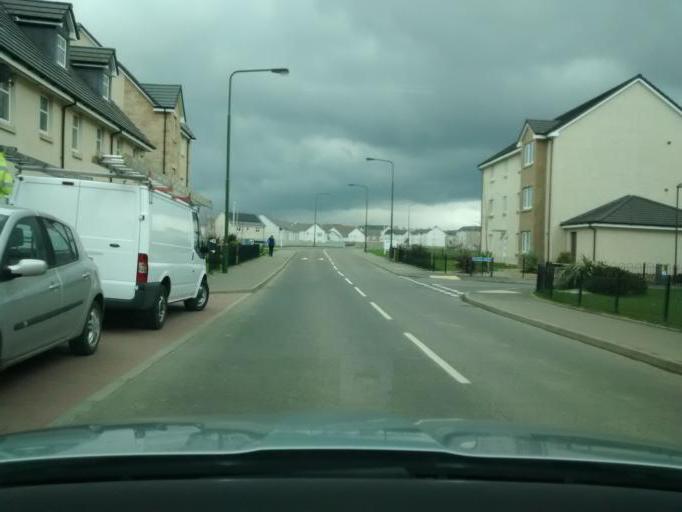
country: GB
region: Scotland
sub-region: West Lothian
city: Bathgate
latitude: 55.8896
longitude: -3.6452
